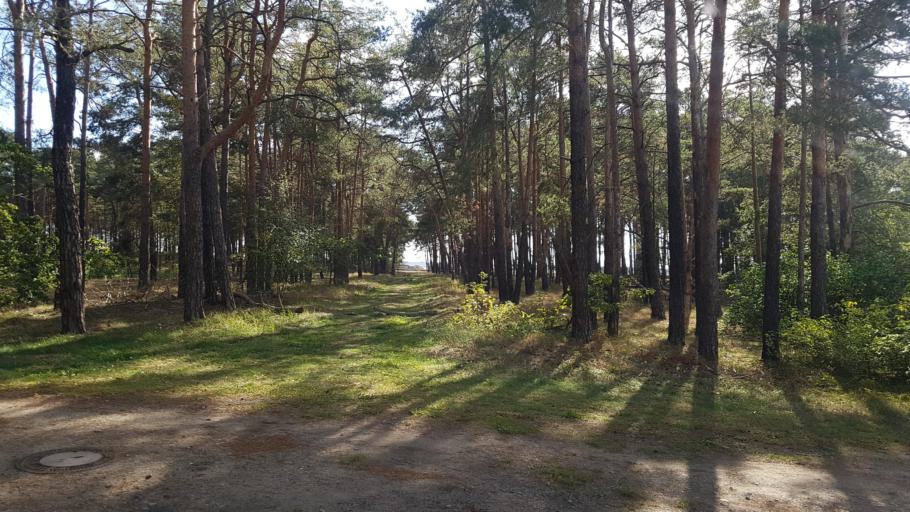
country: DE
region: Brandenburg
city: Peitz
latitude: 51.8076
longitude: 14.4189
